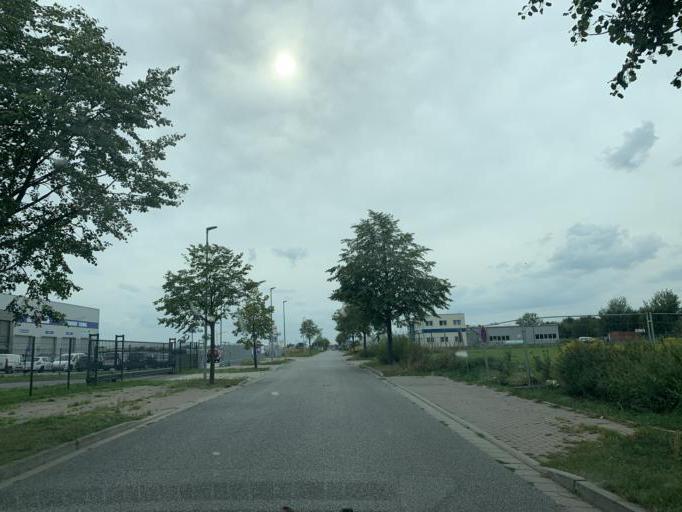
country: DE
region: Brandenburg
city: Velten
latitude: 52.7106
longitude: 13.1143
